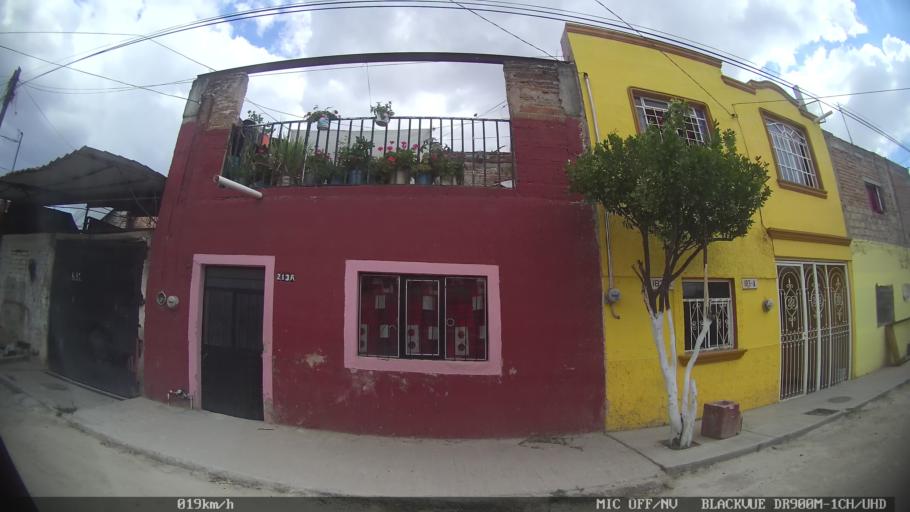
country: MX
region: Jalisco
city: Tlaquepaque
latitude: 20.6824
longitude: -103.2602
